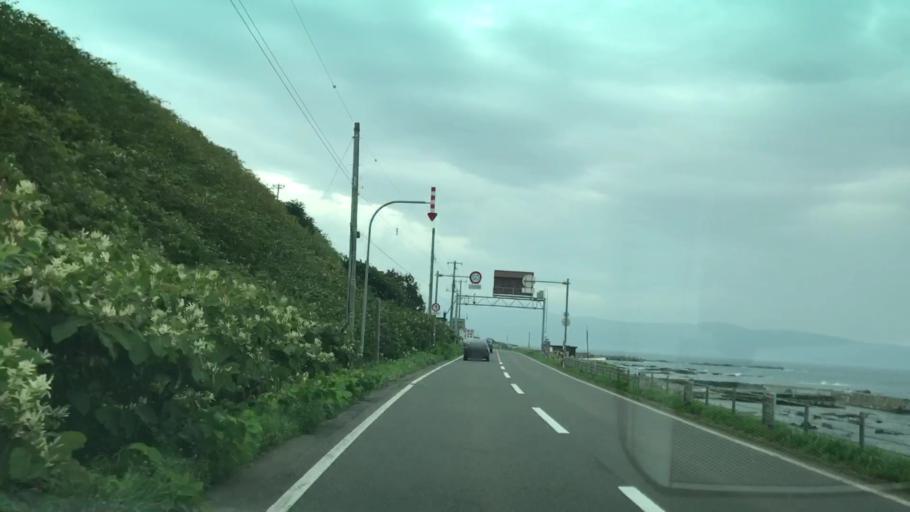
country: JP
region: Hokkaido
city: Iwanai
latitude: 42.8355
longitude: 140.3150
